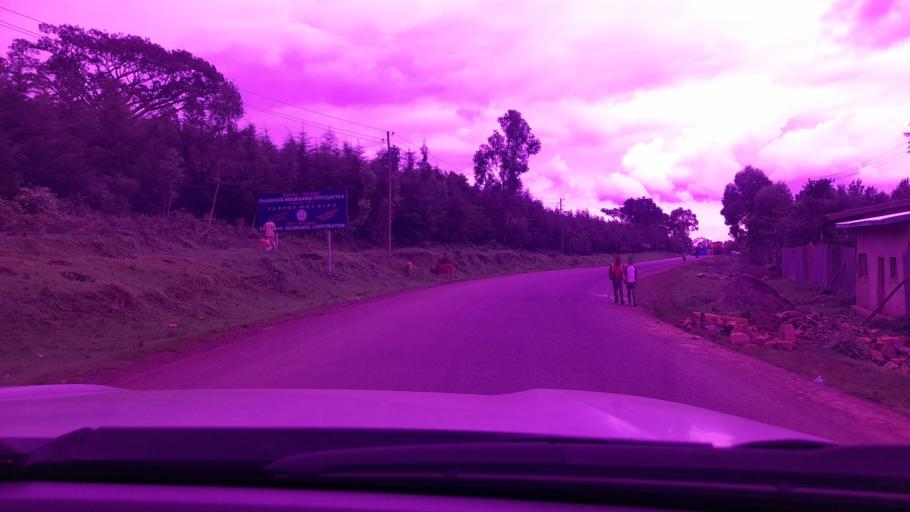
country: ET
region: Oromiya
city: Jima
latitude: 7.6674
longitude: 36.8718
